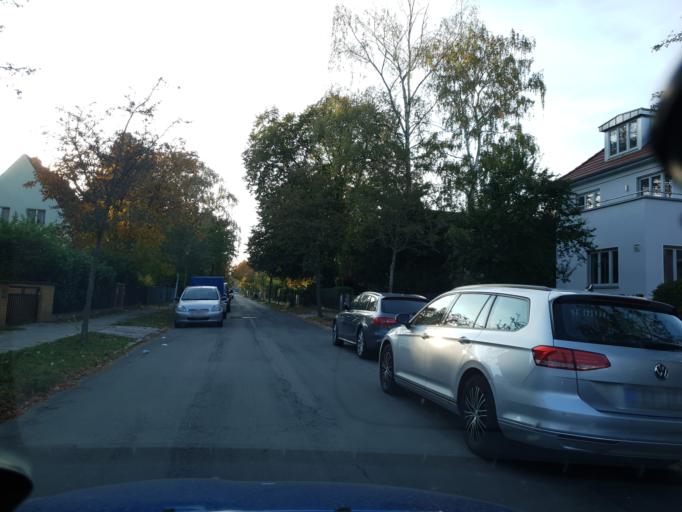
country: DE
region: Berlin
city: Lichtenrade
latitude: 52.3870
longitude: 13.4176
